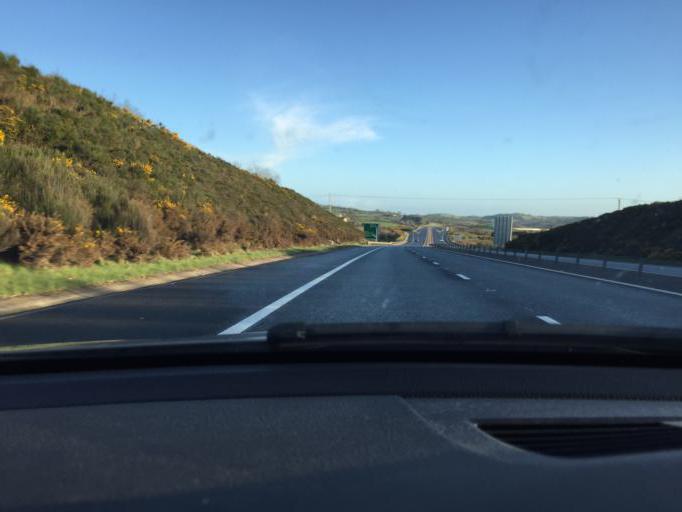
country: GB
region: Northern Ireland
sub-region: Newry and Mourne District
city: Newry
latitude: 54.1928
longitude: -6.3614
